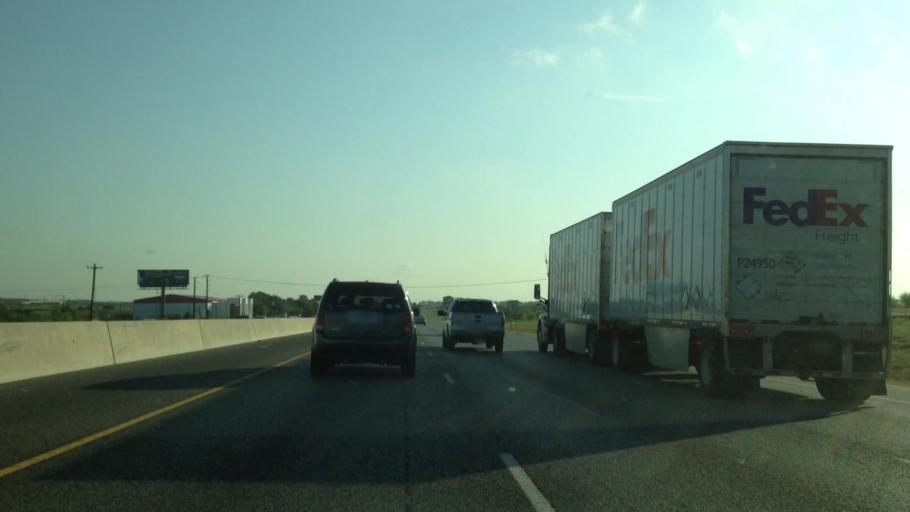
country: US
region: Texas
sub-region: Guadalupe County
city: Redwood
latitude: 29.8078
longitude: -98.0067
